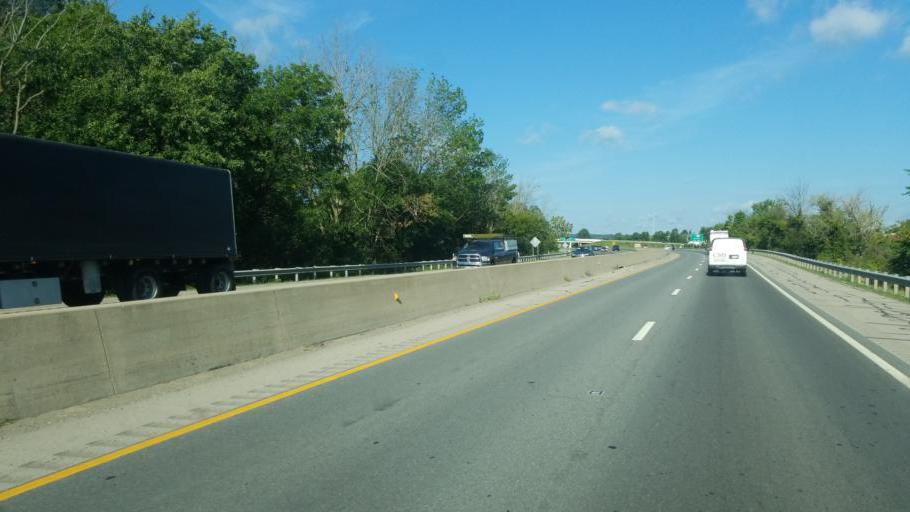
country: US
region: Ohio
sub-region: Wayne County
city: Wooster
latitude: 40.7927
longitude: -81.9438
